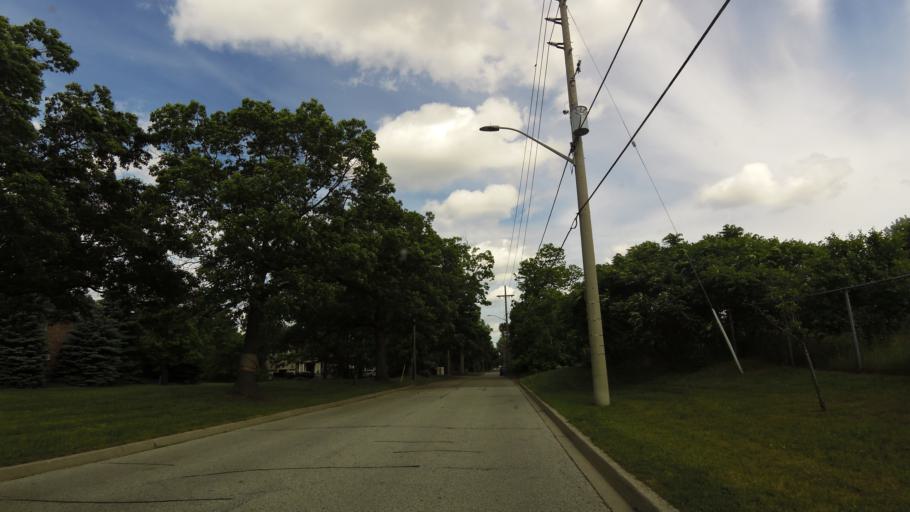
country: CA
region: Ontario
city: Mississauga
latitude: 43.5353
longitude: -79.6471
